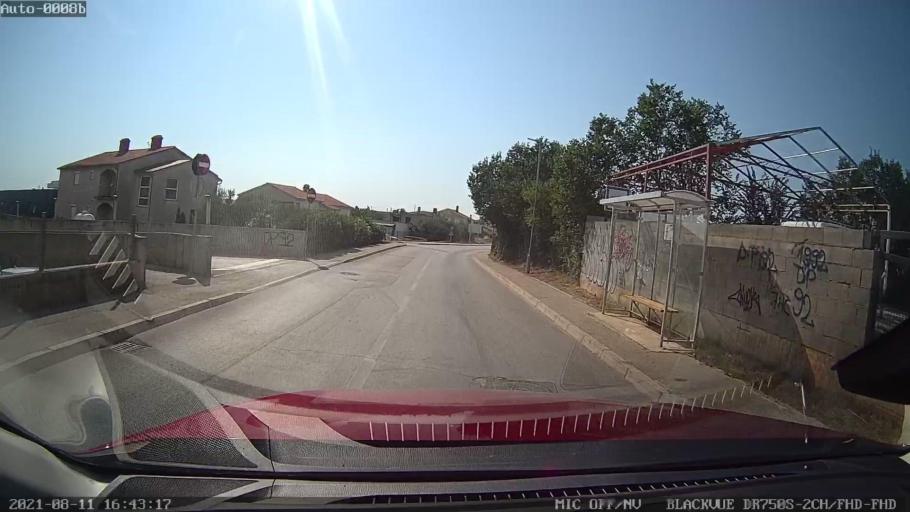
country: HR
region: Istarska
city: Vodnjan
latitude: 44.9541
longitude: 13.8533
